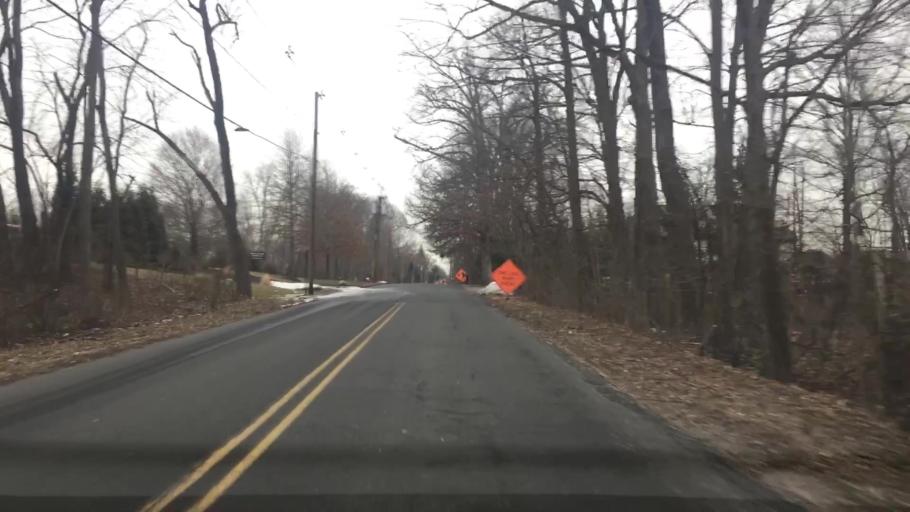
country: US
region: Connecticut
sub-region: Hartford County
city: Kensington
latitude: 41.6204
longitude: -72.7662
